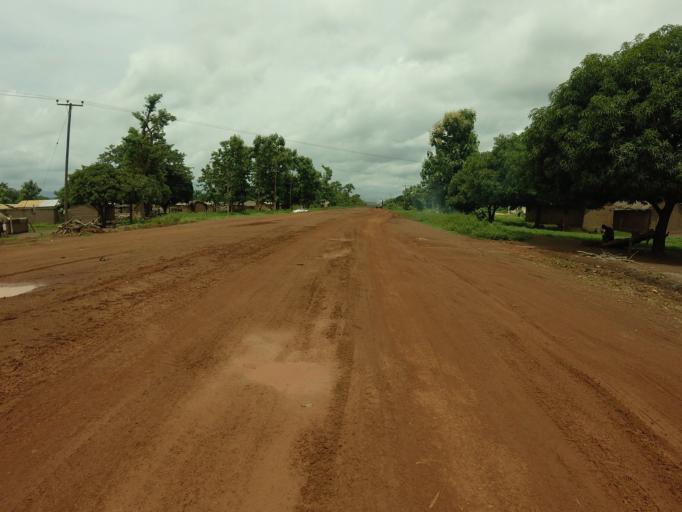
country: GH
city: Kpandae
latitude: 8.4139
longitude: 0.3918
